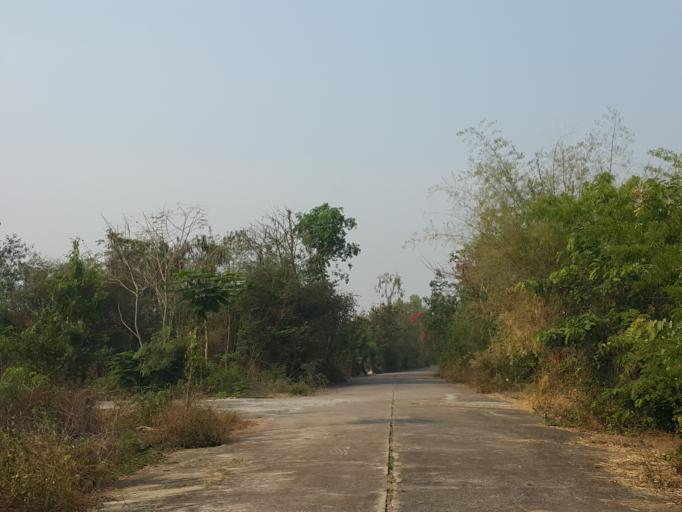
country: TH
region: Chiang Mai
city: San Kamphaeng
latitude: 18.7565
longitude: 99.1067
